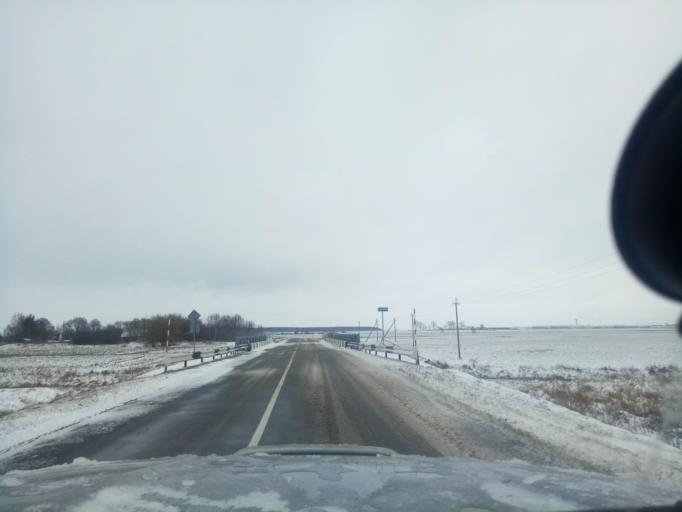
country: BY
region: Minsk
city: Klyetsk
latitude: 53.0078
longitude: 26.6864
